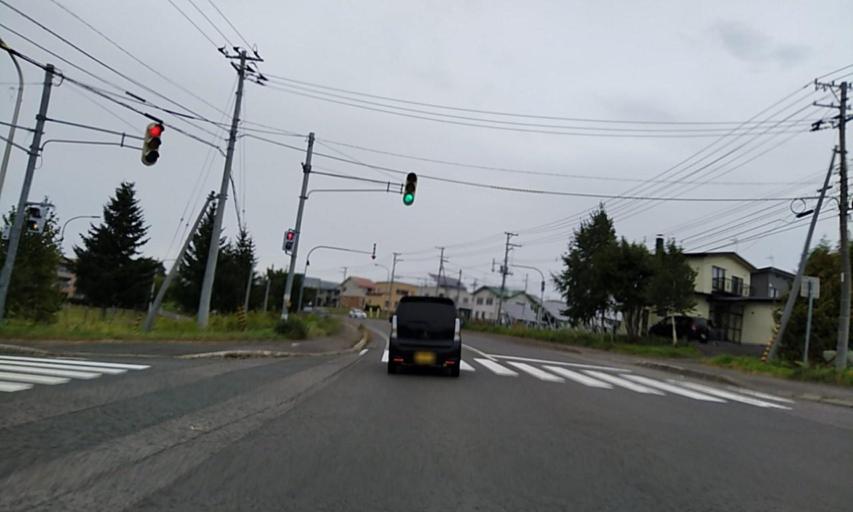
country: JP
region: Hokkaido
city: Bihoro
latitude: 43.9125
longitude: 144.1823
